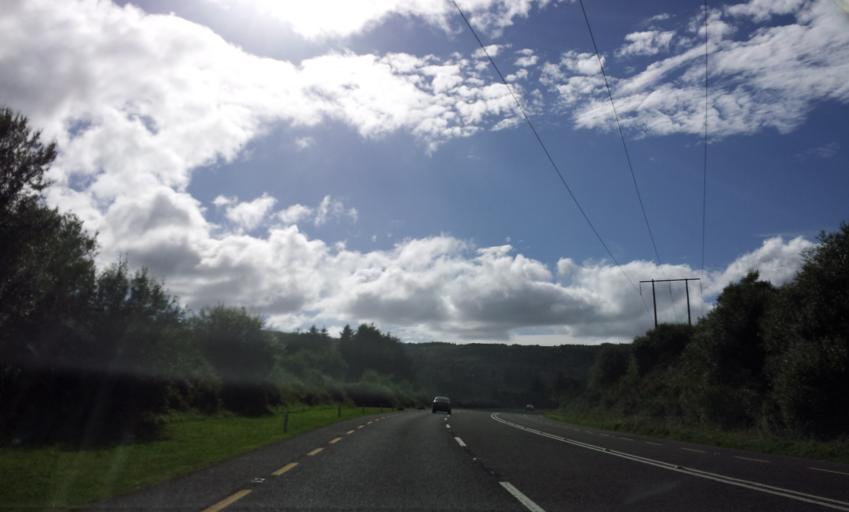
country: IE
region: Munster
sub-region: County Cork
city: Millstreet
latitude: 51.9611
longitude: -9.2326
